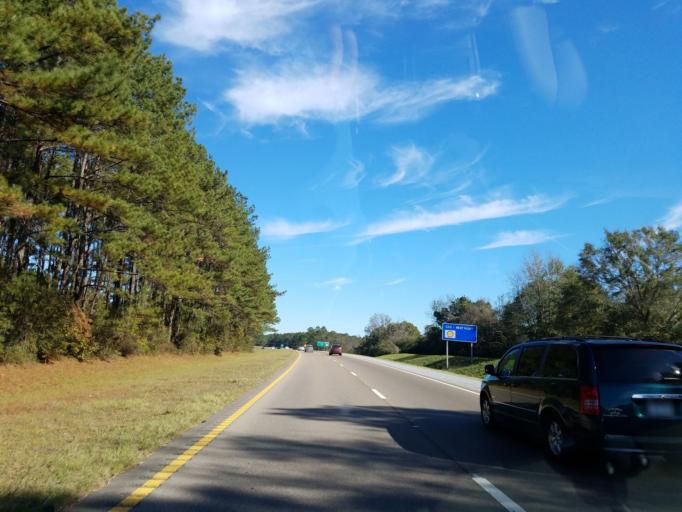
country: US
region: Mississippi
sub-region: Forrest County
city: Hattiesburg
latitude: 31.2379
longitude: -89.3096
